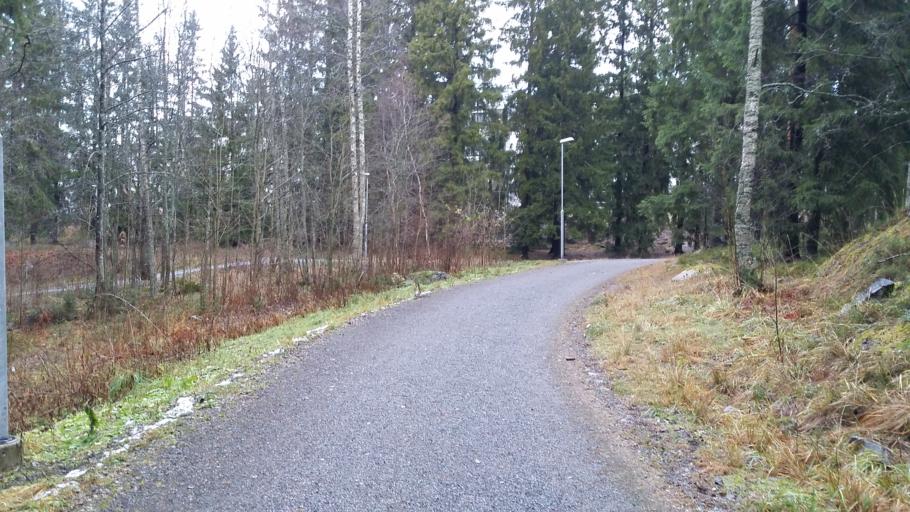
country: FI
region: Pirkanmaa
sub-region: Tampere
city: Pirkkala
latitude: 61.5052
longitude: 23.6366
